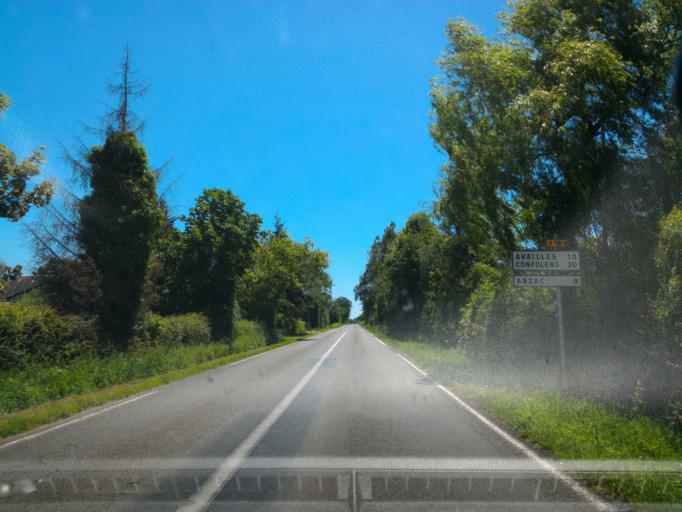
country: FR
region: Poitou-Charentes
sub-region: Departement de la Vienne
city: Availles-Limouzine
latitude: 46.1848
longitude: 0.7254
